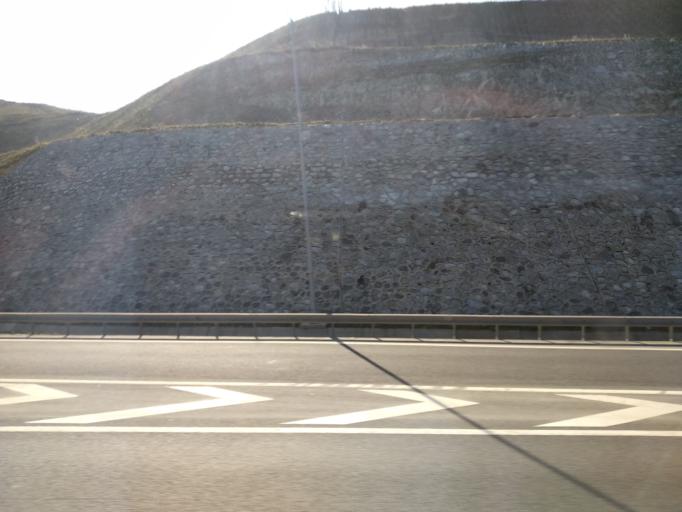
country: TR
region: Istanbul
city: Arikoey
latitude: 41.2259
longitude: 28.9829
